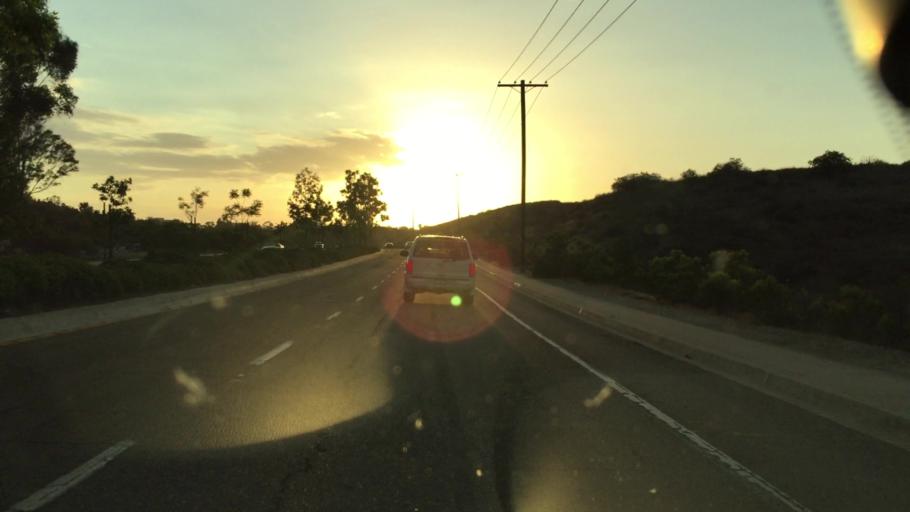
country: US
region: California
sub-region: San Diego County
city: La Mesa
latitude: 32.8329
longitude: -117.1133
